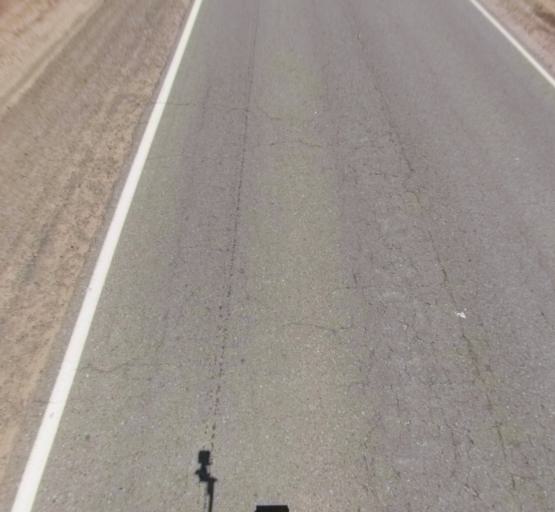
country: US
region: California
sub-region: Madera County
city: Fairmead
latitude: 37.0401
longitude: -120.2060
